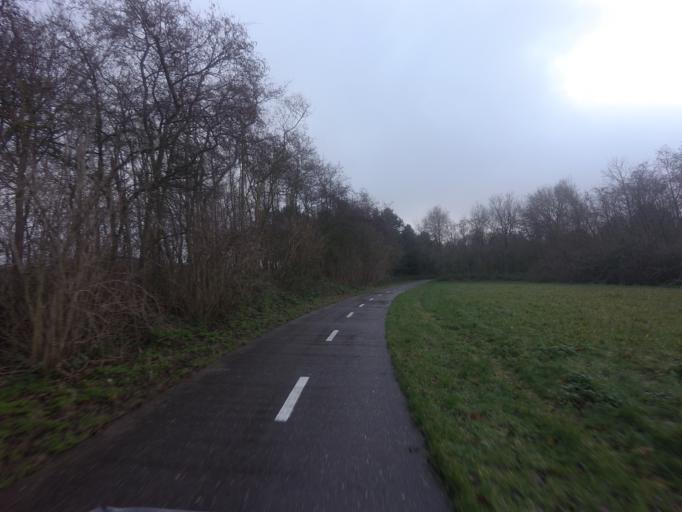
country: NL
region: North Holland
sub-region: Gemeente Texel
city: Den Burg
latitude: 53.1565
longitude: 4.8624
